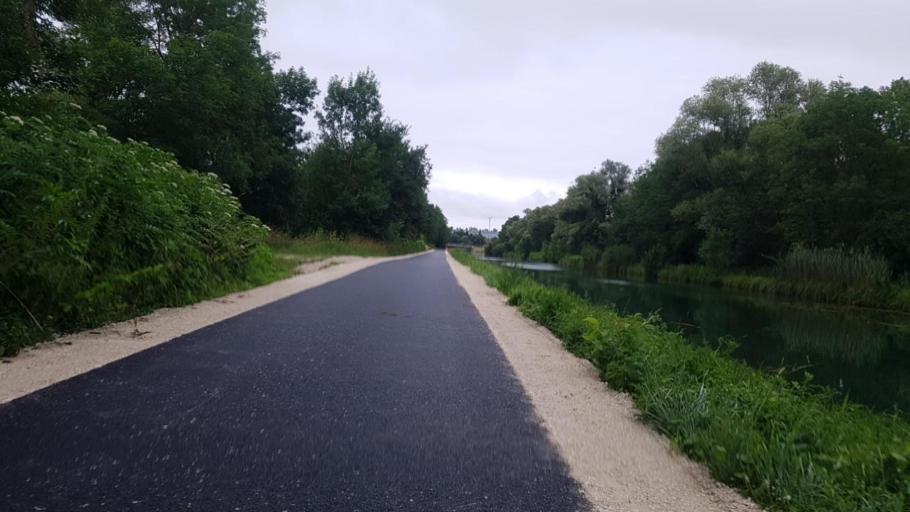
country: FR
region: Champagne-Ardenne
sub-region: Departement de la Marne
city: Vitry-le-Francois
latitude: 48.8298
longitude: 4.5132
